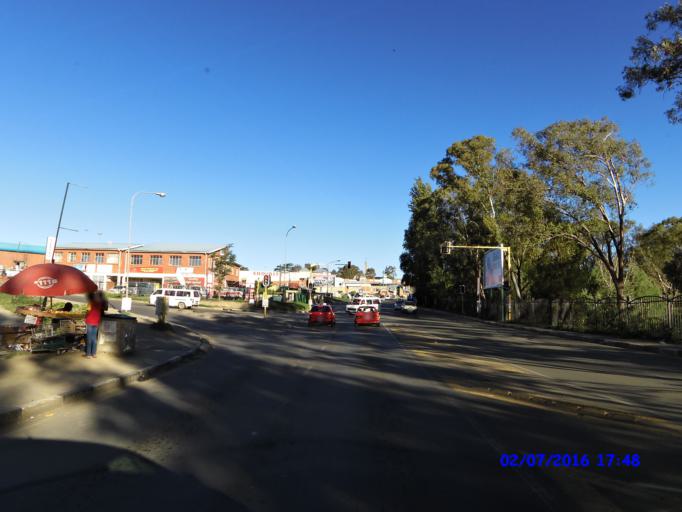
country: LS
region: Maseru
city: Maseru
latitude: -29.3129
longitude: 27.4909
